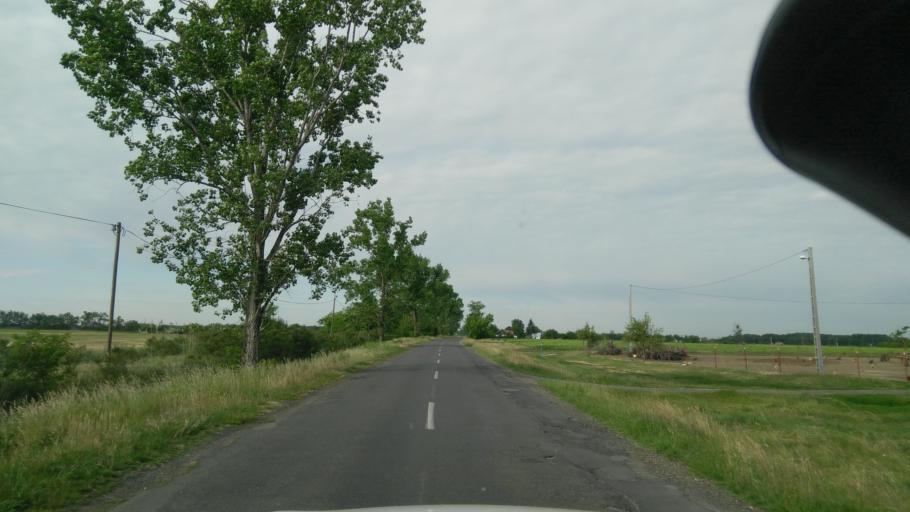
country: HU
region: Bekes
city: Gyula
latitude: 46.6041
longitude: 21.2408
